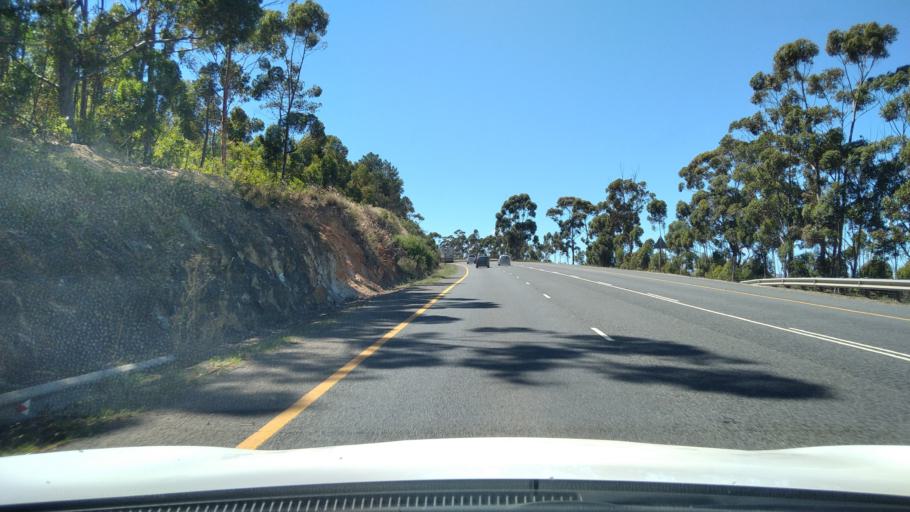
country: ZA
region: Western Cape
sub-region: Overberg District Municipality
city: Caledon
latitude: -34.2196
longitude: 19.4048
